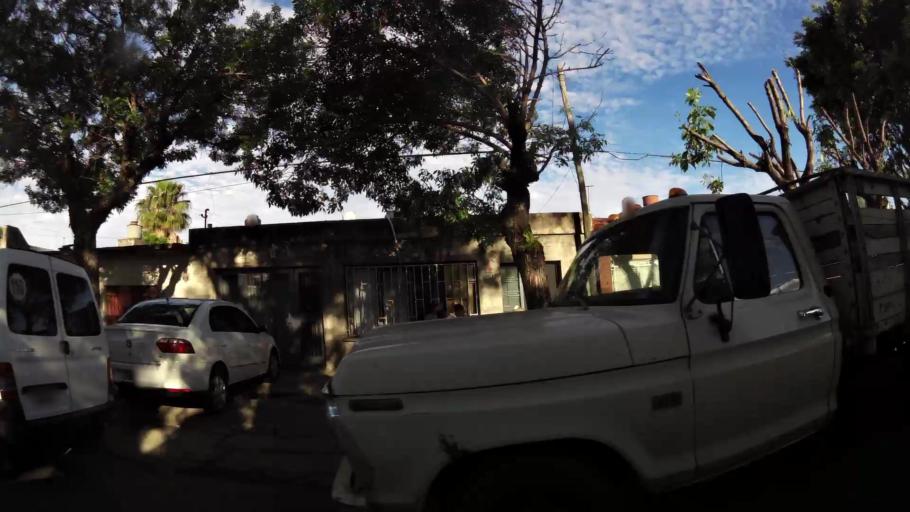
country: AR
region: Santa Fe
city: Gobernador Galvez
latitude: -32.9899
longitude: -60.6692
